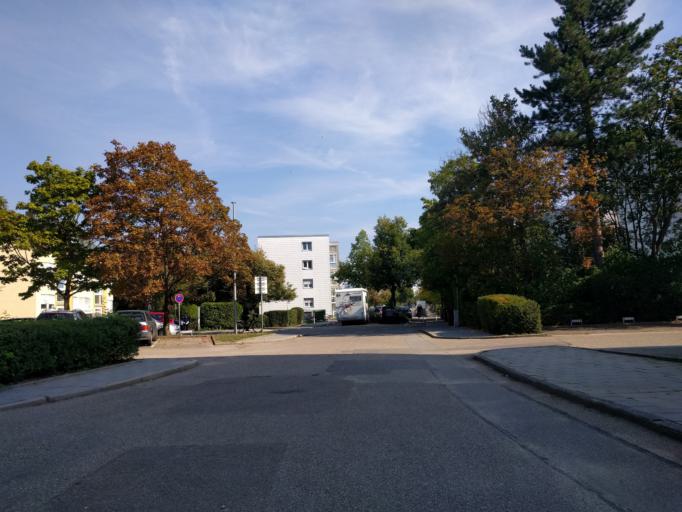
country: DE
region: Bavaria
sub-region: Upper Palatinate
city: Regensburg
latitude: 49.0232
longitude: 12.1221
